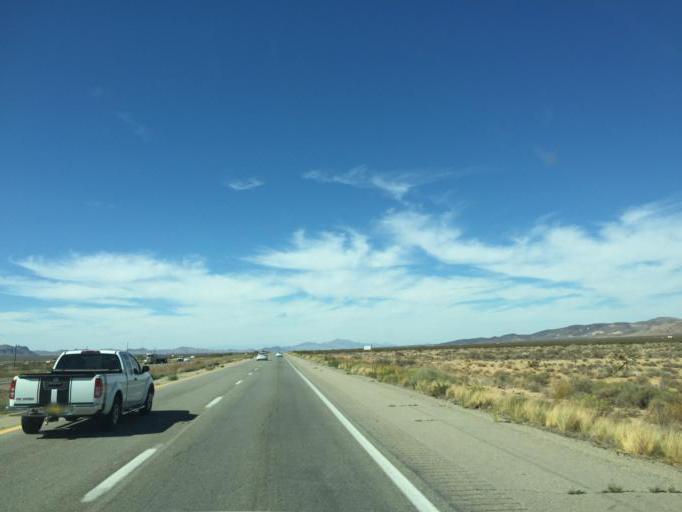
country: US
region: Arizona
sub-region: Mohave County
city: Dolan Springs
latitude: 35.5619
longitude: -114.3746
